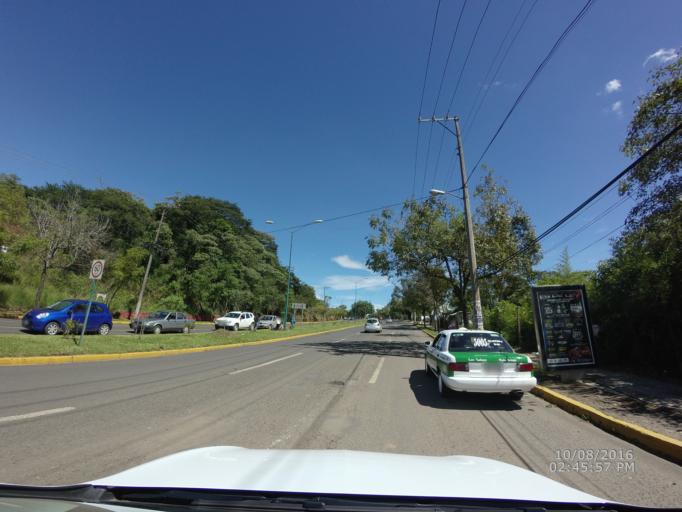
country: MX
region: Veracruz
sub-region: Xalapa
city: Lomas Verdes
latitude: 19.5057
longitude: -96.8964
